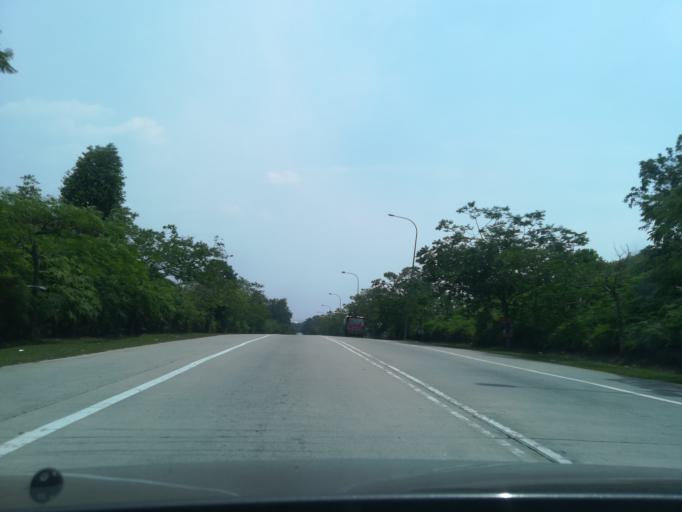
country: MY
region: Kedah
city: Kulim
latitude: 5.4171
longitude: 100.5668
